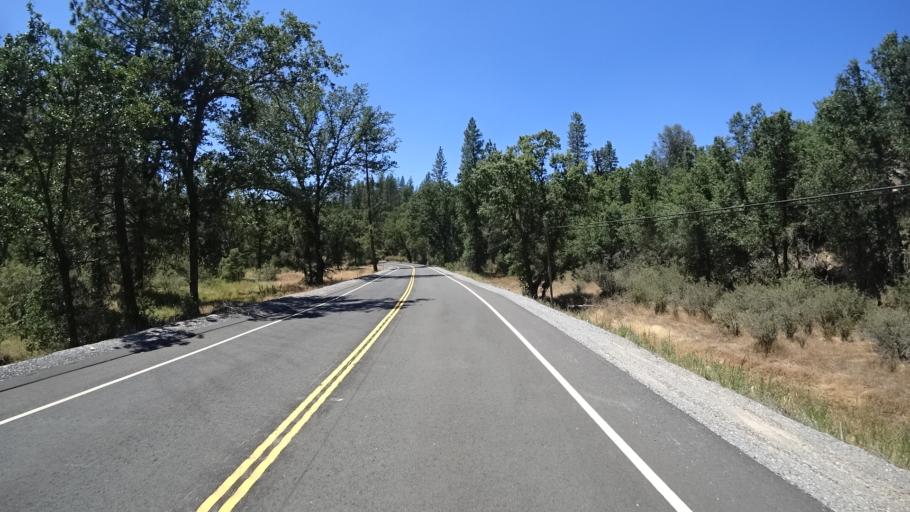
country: US
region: California
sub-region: Calaveras County
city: Mountain Ranch
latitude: 38.2959
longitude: -120.4969
